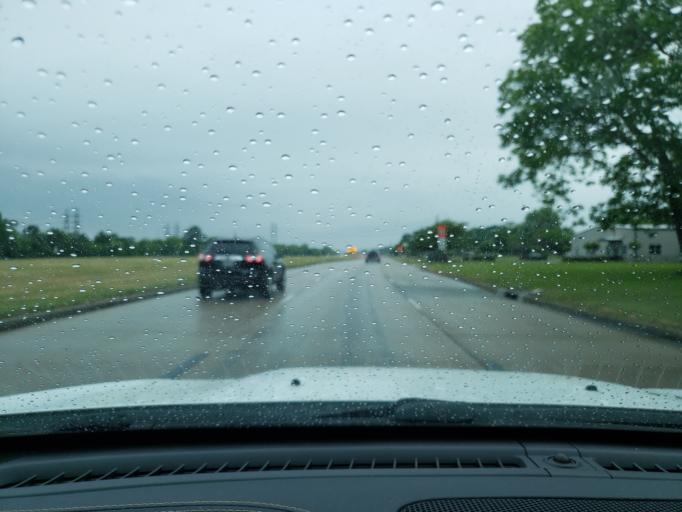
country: US
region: Texas
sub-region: Harris County
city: Baytown
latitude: 29.7574
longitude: -94.9312
